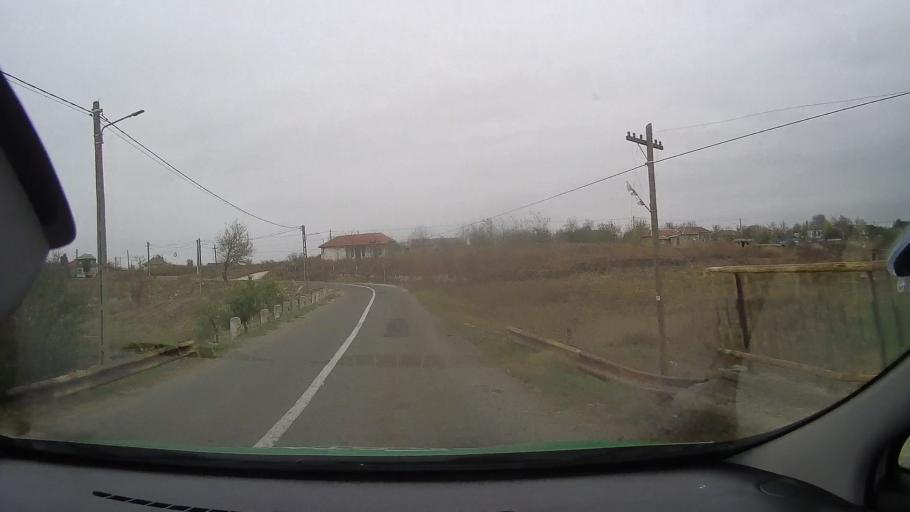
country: RO
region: Constanta
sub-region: Comuna Vulturu
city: Vulturu
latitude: 44.7004
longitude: 28.2404
